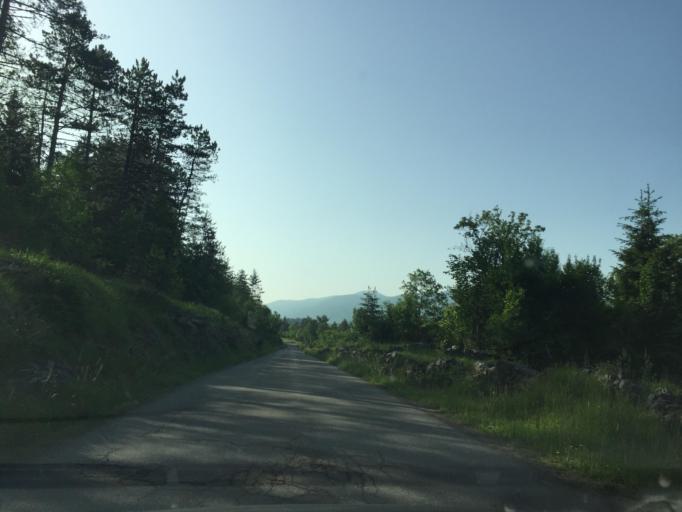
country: HR
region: Istarska
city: Buzet
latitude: 45.4562
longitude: 14.1436
